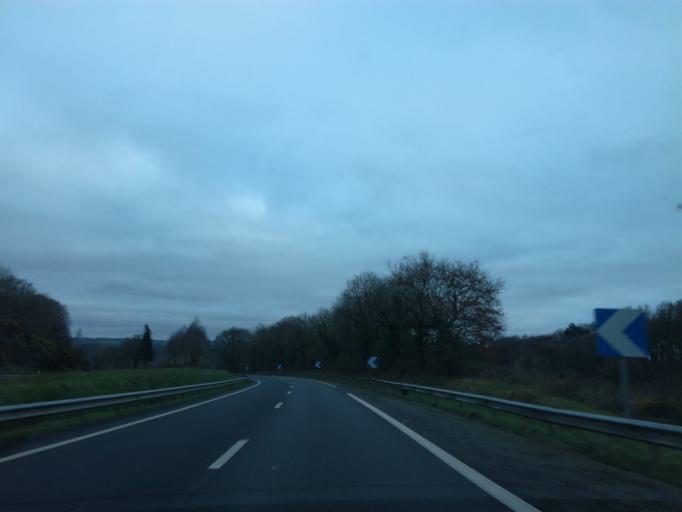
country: FR
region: Brittany
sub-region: Departement des Cotes-d'Armor
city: Plemet
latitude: 48.1688
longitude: -2.6475
